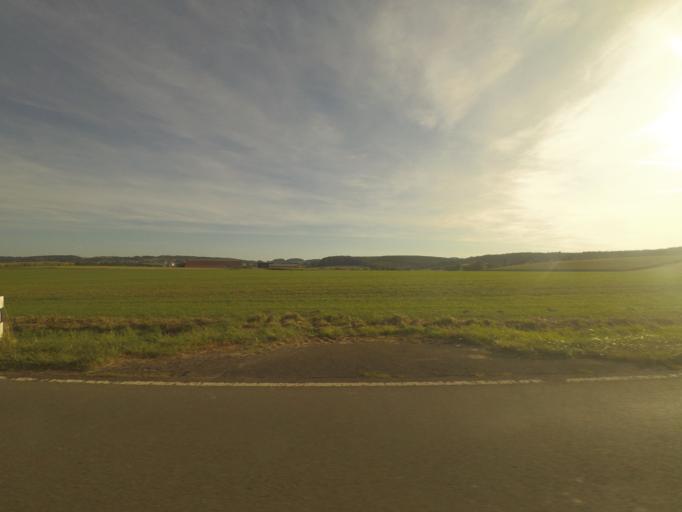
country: DE
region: Hesse
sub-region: Regierungsbezirk Kassel
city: Flieden
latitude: 50.4233
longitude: 9.5459
